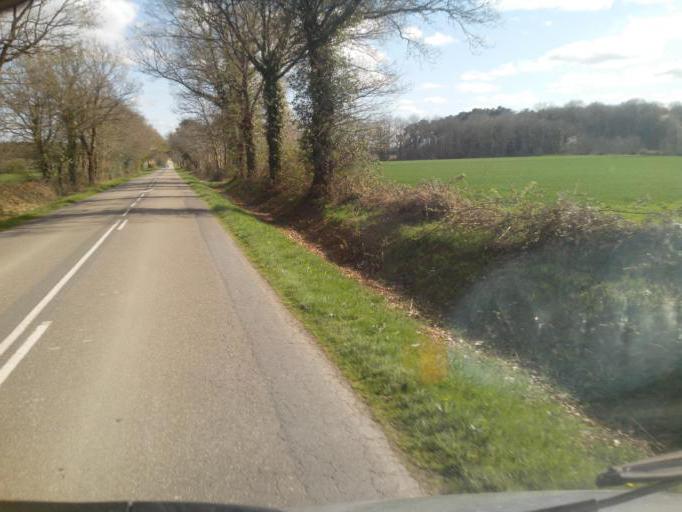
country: FR
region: Brittany
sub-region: Departement d'Ille-et-Vilaine
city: Maxent
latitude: 47.9570
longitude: -2.0134
